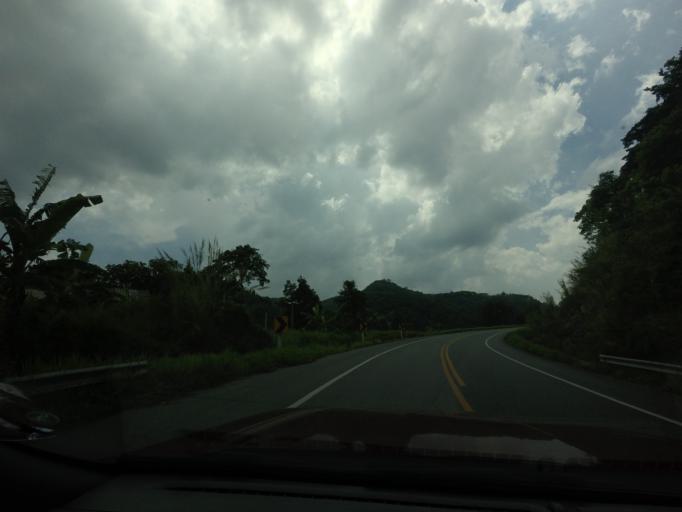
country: TH
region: Yala
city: Than To
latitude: 6.0547
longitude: 101.1933
